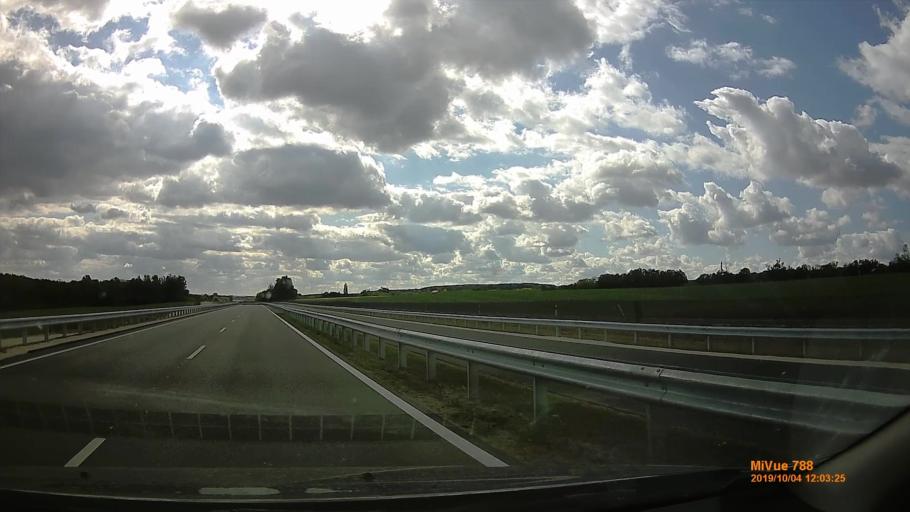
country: HU
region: Somogy
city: Karad
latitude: 46.5877
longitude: 17.8030
